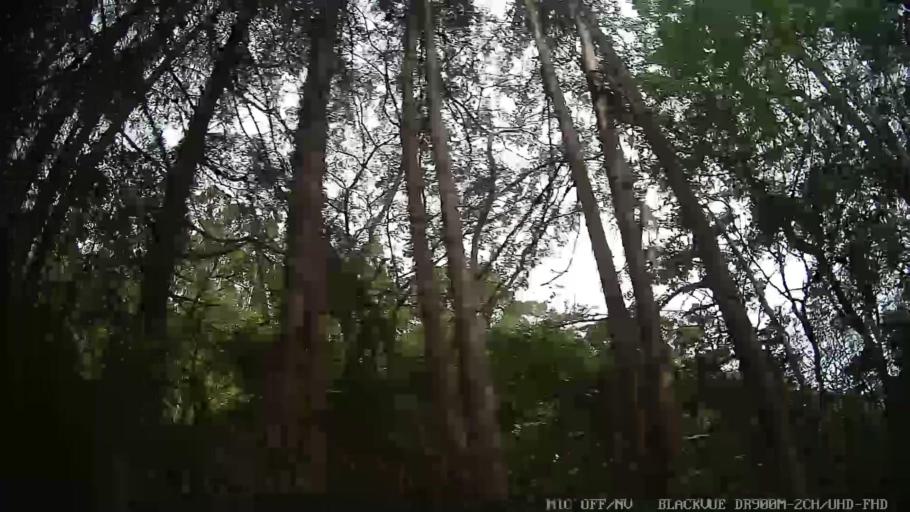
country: BR
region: Sao Paulo
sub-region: Itatiba
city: Itatiba
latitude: -23.0340
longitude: -46.8941
